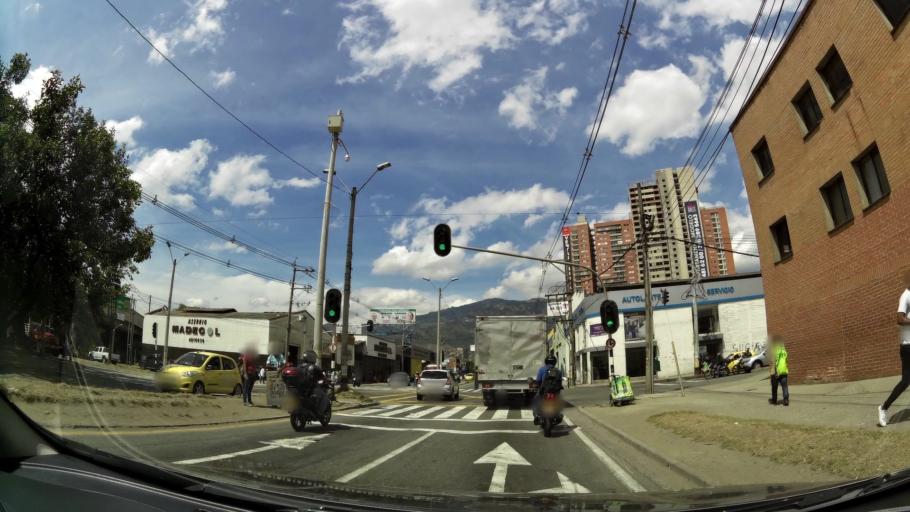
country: CO
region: Antioquia
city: Bello
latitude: 6.3368
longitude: -75.5476
